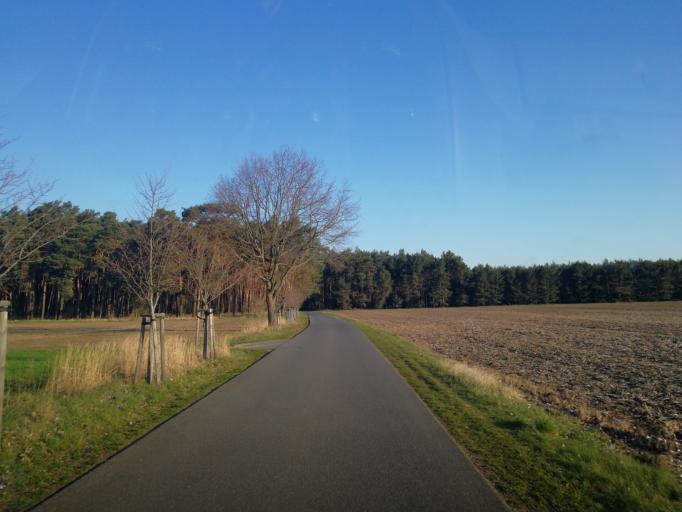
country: DE
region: Brandenburg
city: Drahnsdorf
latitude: 51.8882
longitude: 13.5809
